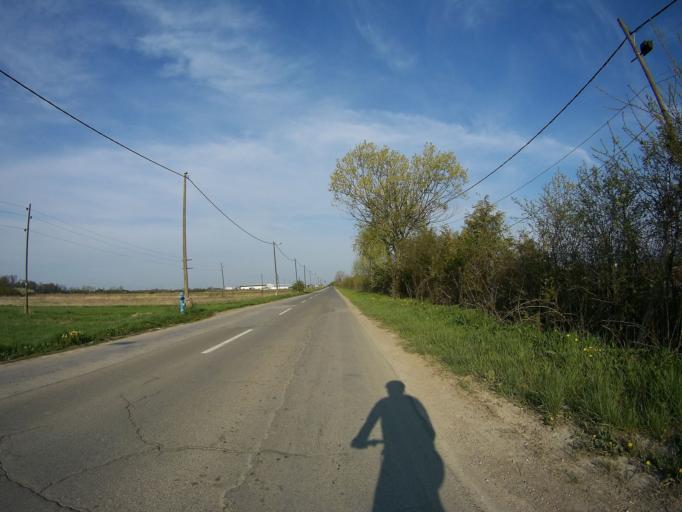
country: HR
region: Zagrebacka
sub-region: Grad Velika Gorica
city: Velika Gorica
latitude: 45.7056
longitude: 16.1090
